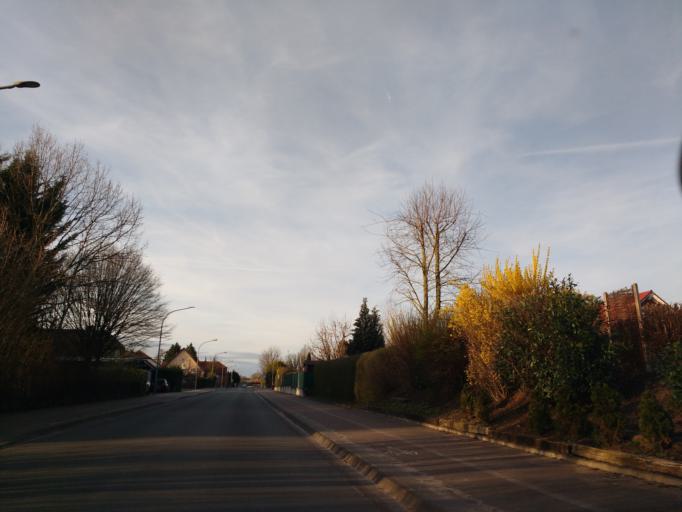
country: DE
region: North Rhine-Westphalia
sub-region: Regierungsbezirk Detmold
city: Salzkotten
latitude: 51.6678
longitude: 8.6156
